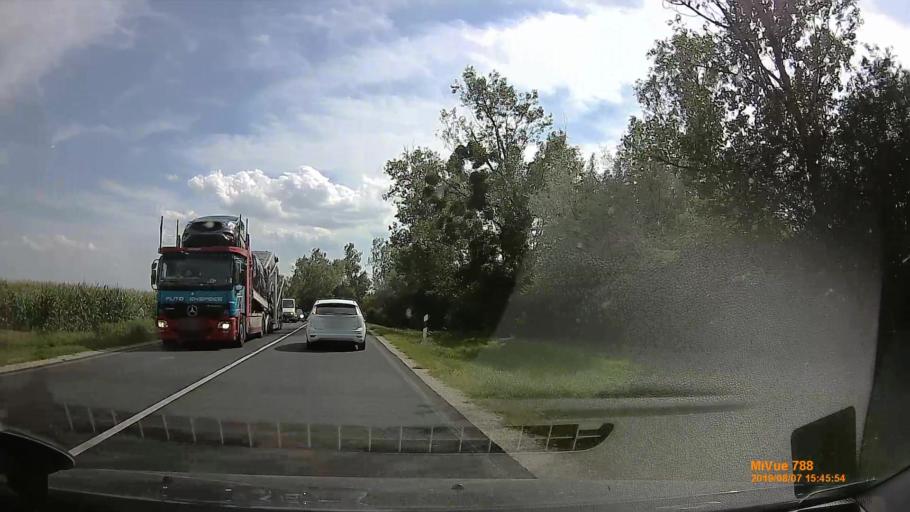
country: HU
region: Vas
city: Szombathely
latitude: 47.1914
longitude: 16.6202
